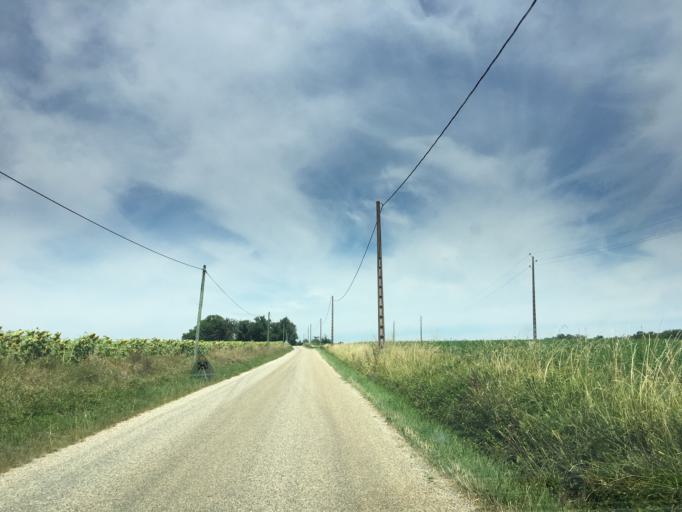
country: FR
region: Midi-Pyrenees
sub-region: Departement du Gers
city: Jegun
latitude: 43.7959
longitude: 0.4943
